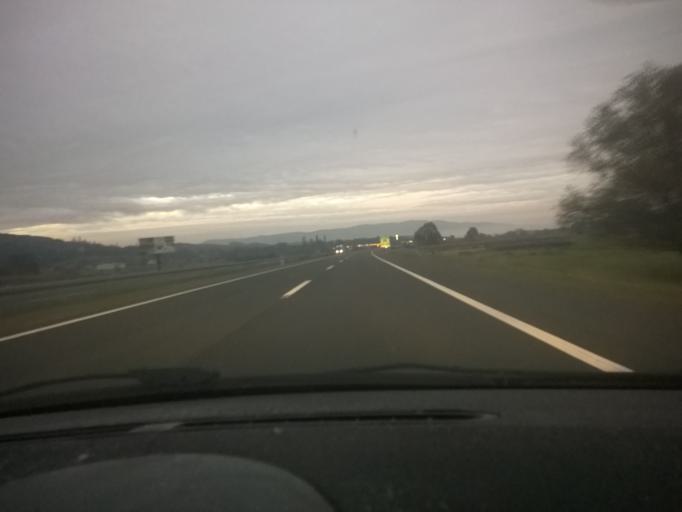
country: HR
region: Krapinsko-Zagorska
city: Zabok
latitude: 46.0745
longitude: 15.9178
